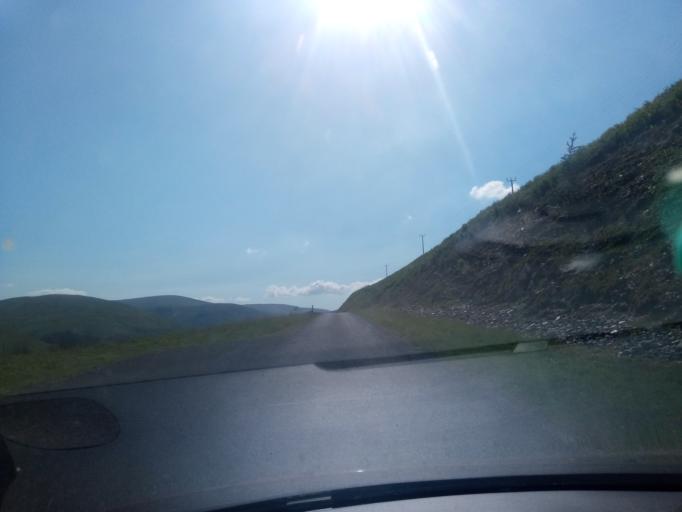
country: GB
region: Scotland
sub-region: The Scottish Borders
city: Peebles
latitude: 55.4949
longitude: -3.2624
